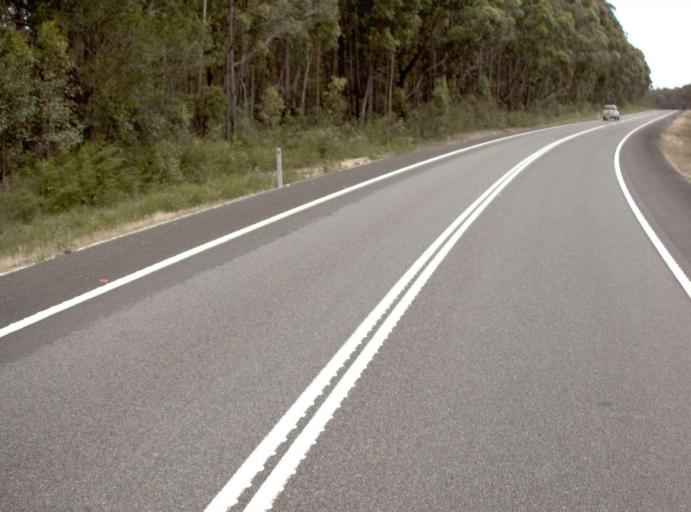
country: AU
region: New South Wales
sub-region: Bega Valley
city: Eden
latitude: -37.5204
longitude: 149.4960
